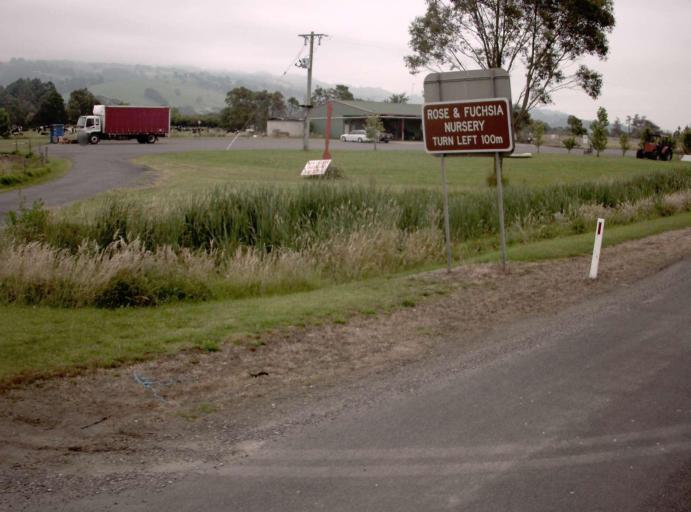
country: AU
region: Victoria
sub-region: Latrobe
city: Moe
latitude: -38.2092
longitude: 146.1304
